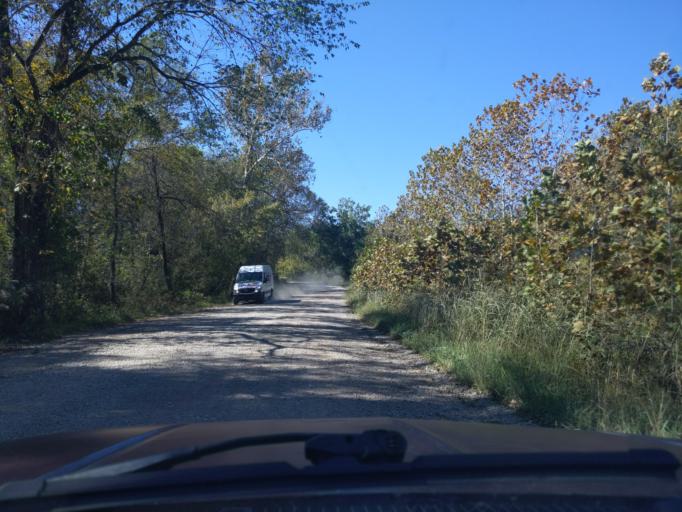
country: US
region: Oklahoma
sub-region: Creek County
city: Bristow
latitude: 35.6842
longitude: -96.4150
